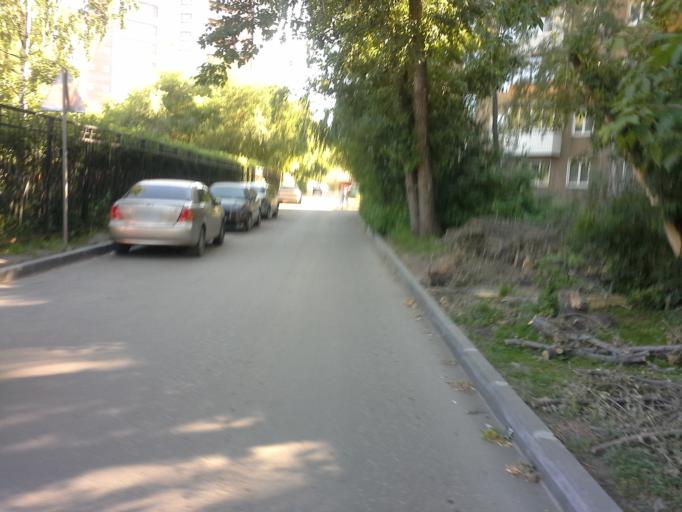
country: RU
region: Novosibirsk
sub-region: Novosibirskiy Rayon
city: Novosibirsk
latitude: 54.9852
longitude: 82.9095
